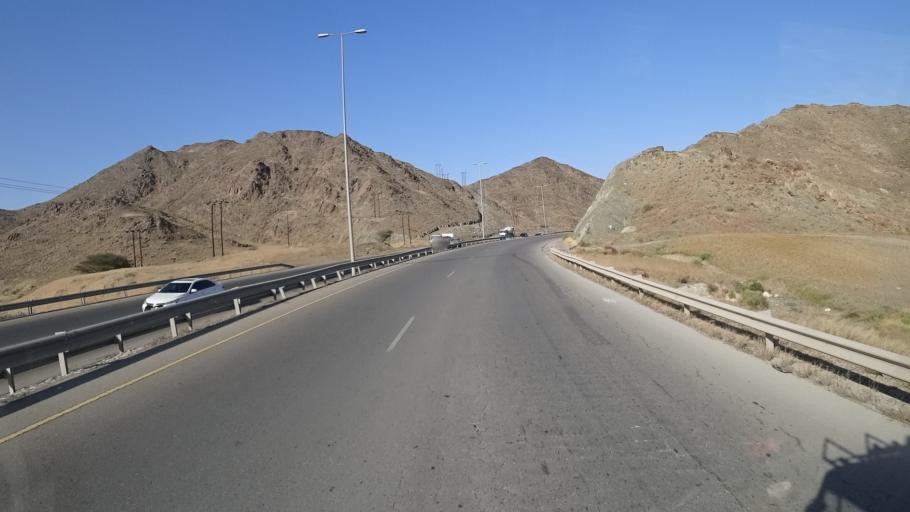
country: OM
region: Muhafazat ad Dakhiliyah
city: Bidbid
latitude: 23.4666
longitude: 58.1896
